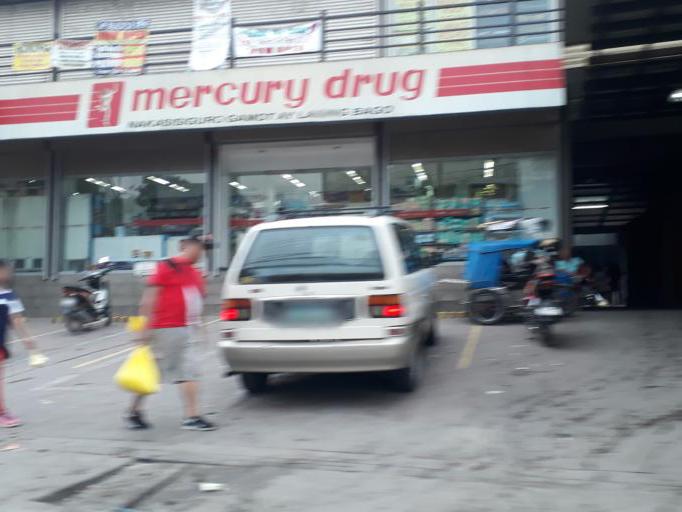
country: PH
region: Calabarzon
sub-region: Province of Rizal
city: Valenzuela
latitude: 14.6871
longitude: 120.9576
